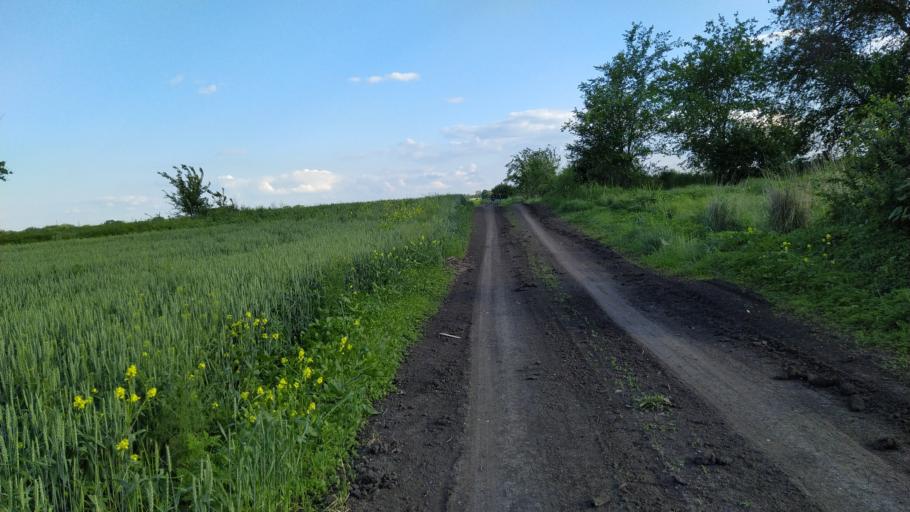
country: RU
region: Rostov
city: Bataysk
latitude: 47.1243
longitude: 39.7227
